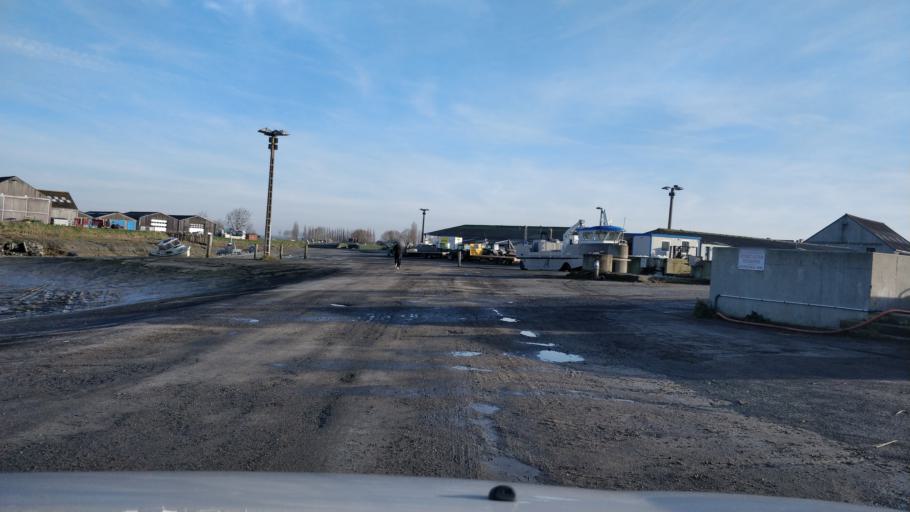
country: FR
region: Brittany
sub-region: Departement d'Ille-et-Vilaine
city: Le Vivier-sur-Mer
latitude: 48.6043
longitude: -1.7713
